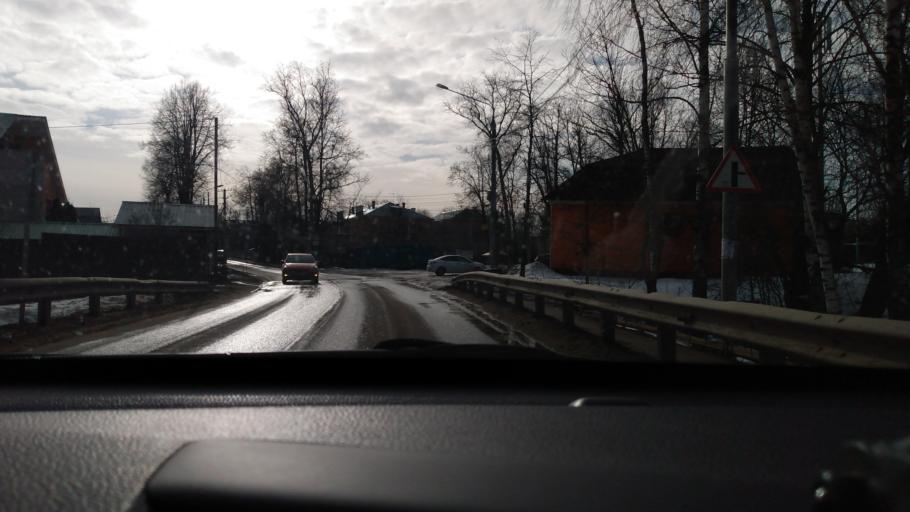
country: RU
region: Moskovskaya
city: Nakhabino
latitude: 55.8667
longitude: 37.1848
